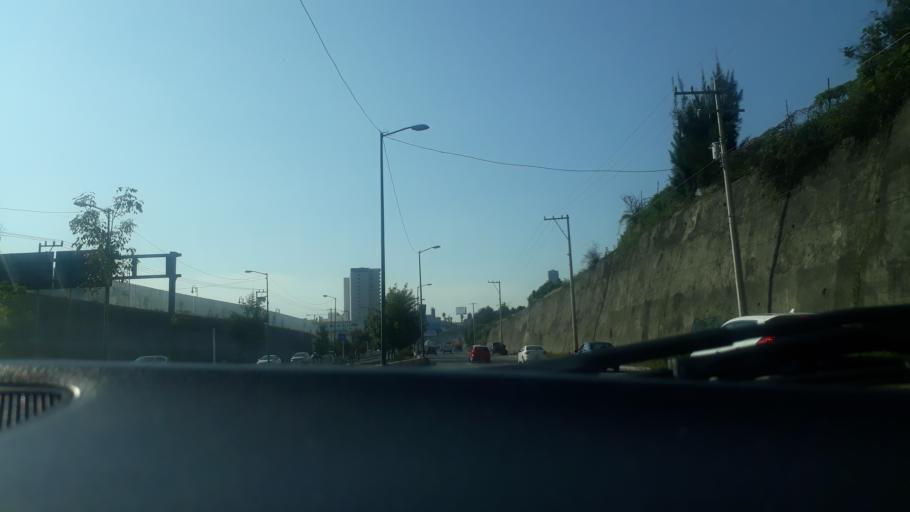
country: MX
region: Puebla
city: Tlazcalancingo
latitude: 18.9962
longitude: -98.2557
